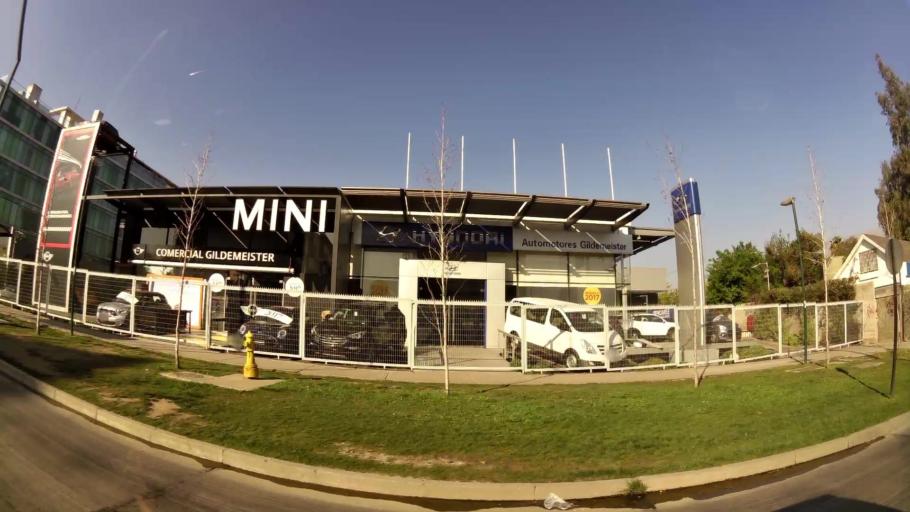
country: CL
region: Santiago Metropolitan
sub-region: Provincia de Santiago
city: Villa Presidente Frei, Nunoa, Santiago, Chile
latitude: -33.3554
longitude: -70.5175
